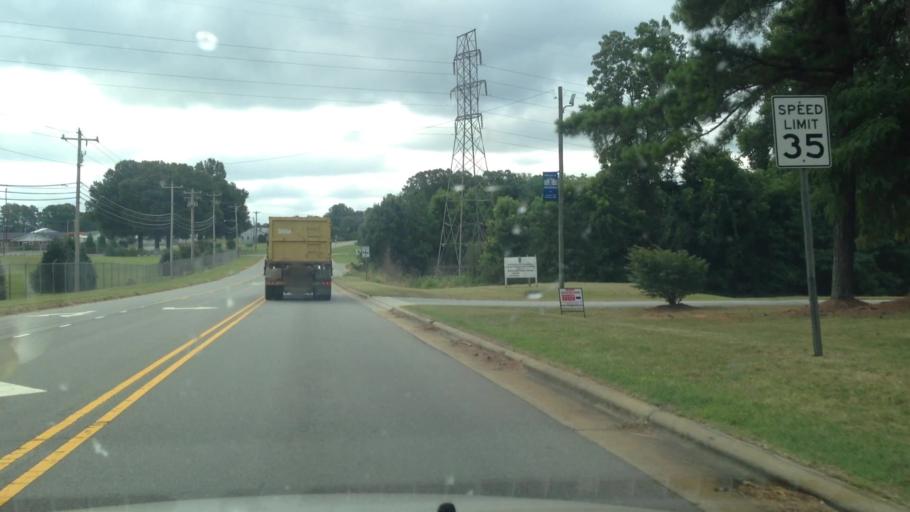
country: US
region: North Carolina
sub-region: Rockingham County
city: Wentworth
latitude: 36.3889
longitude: -79.7497
